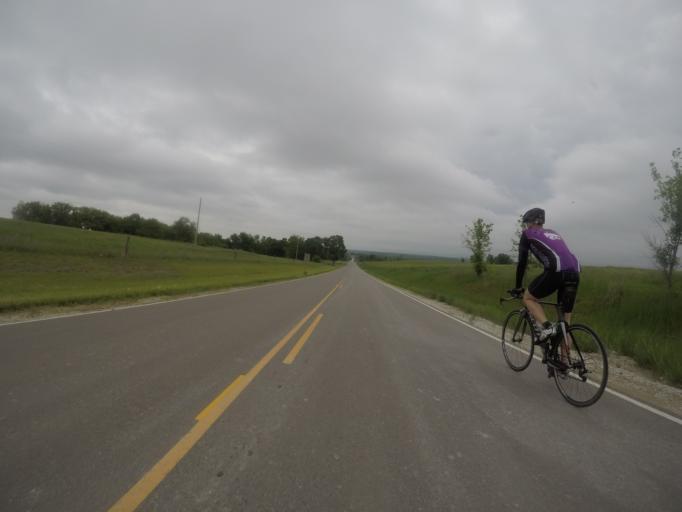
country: US
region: Kansas
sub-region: Pottawatomie County
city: Westmoreland
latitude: 39.5078
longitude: -96.1743
